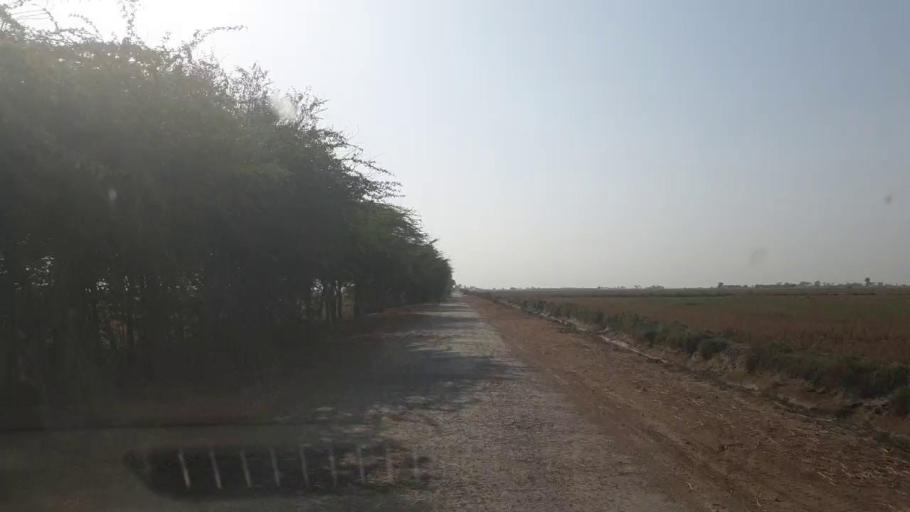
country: PK
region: Sindh
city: Kario
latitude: 24.5765
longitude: 68.5199
